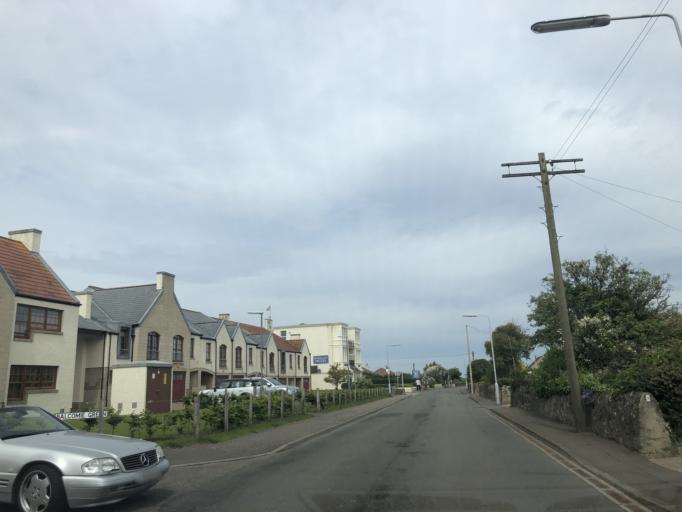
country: GB
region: Scotland
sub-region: Fife
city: Anstruther
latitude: 56.2637
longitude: -2.6223
